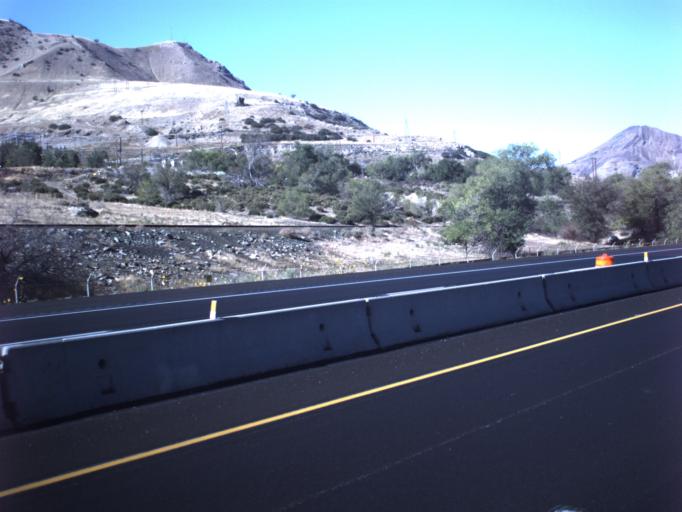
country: US
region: Utah
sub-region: Salt Lake County
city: Magna
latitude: 40.7178
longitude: -112.1373
